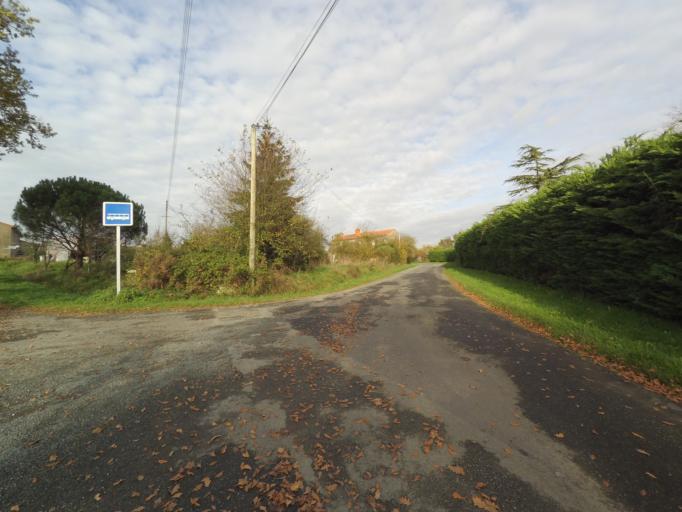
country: FR
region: Pays de la Loire
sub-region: Departement de la Loire-Atlantique
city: Saint-Hilaire-de-Clisson
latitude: 47.0397
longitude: -1.3371
